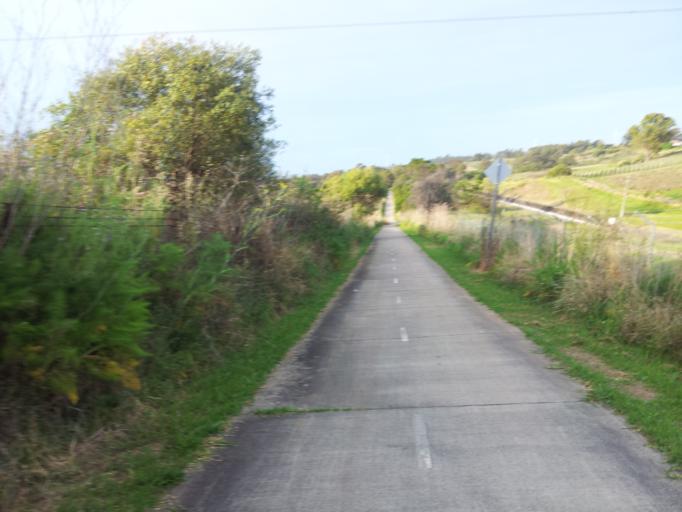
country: AU
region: New South Wales
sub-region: Fairfield
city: Horsley Park
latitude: -33.8351
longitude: 150.8781
